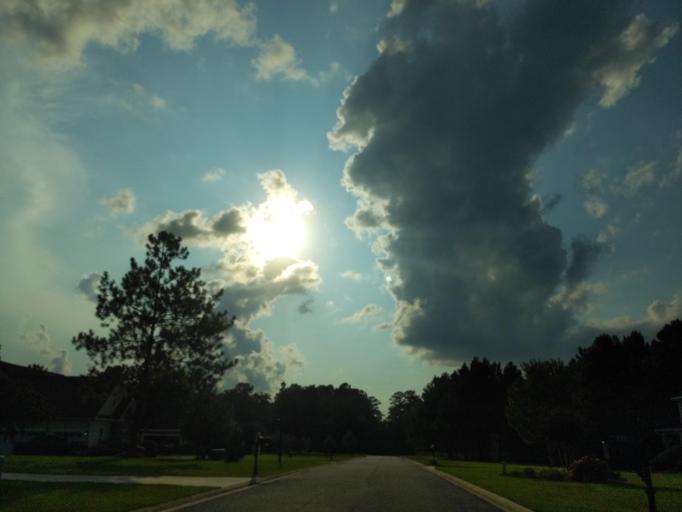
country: US
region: Georgia
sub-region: Thomas County
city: Thomasville
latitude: 30.8983
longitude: -83.9434
